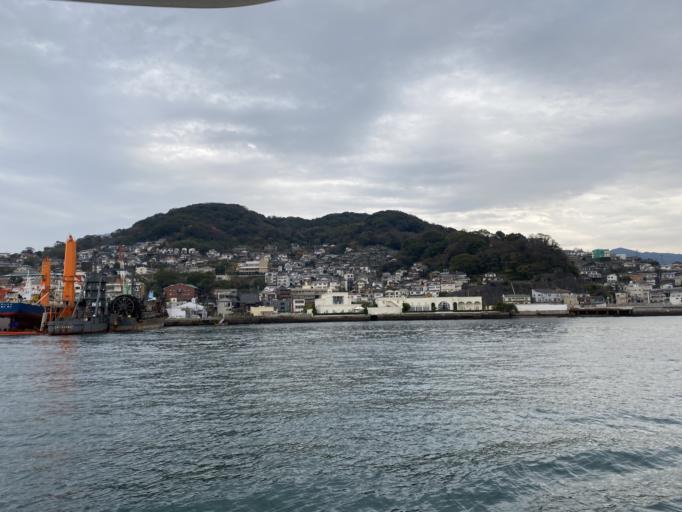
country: JP
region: Nagasaki
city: Nagasaki-shi
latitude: 32.7331
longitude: 129.8619
